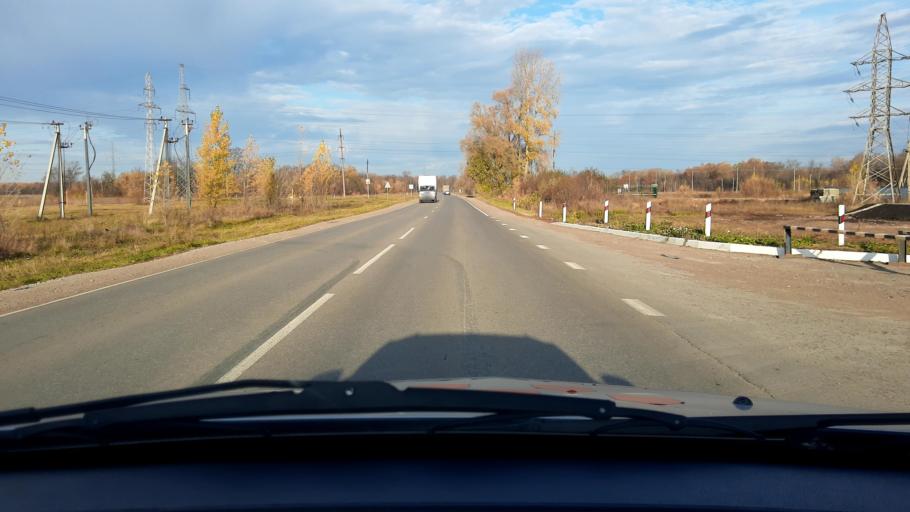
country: RU
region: Bashkortostan
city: Mikhaylovka
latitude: 54.8007
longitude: 55.8354
